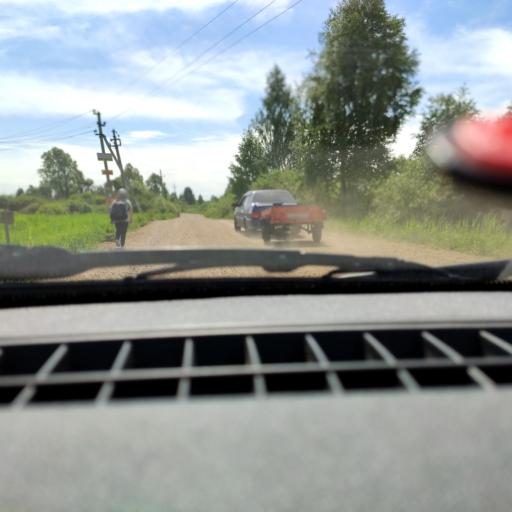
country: RU
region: Bashkortostan
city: Kabakovo
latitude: 54.7305
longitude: 56.2012
